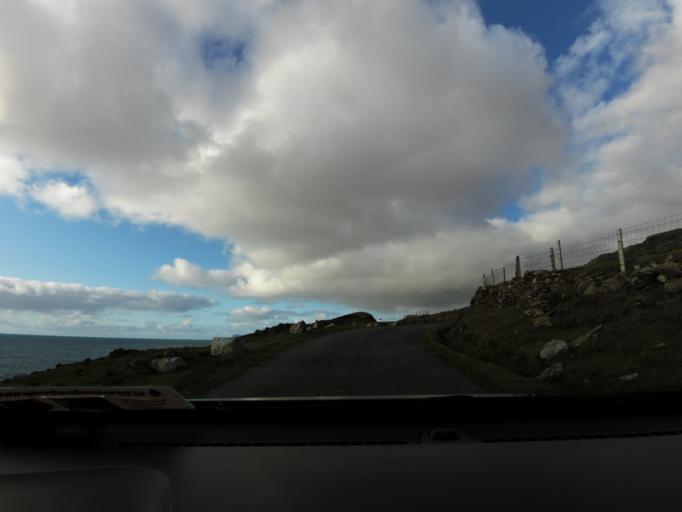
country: IE
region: Connaught
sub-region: Maigh Eo
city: Belmullet
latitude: 53.8778
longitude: -9.9664
